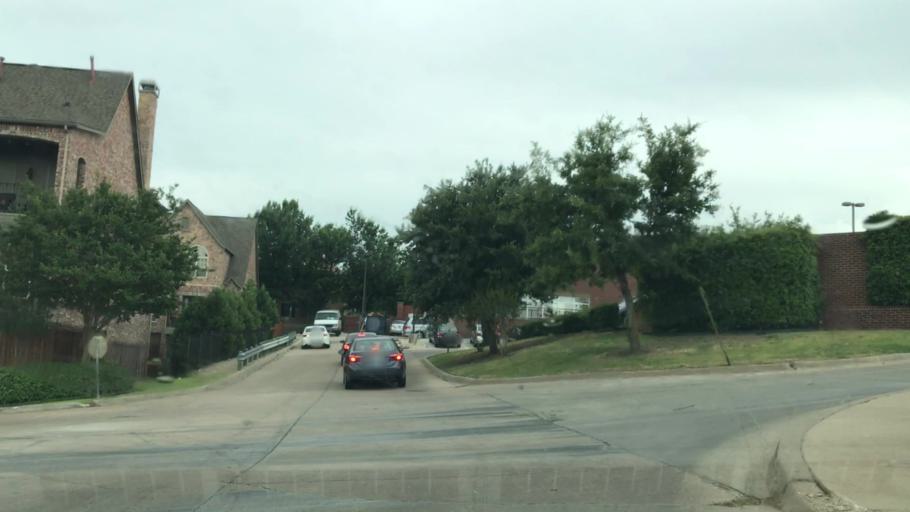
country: US
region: Texas
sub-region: Dallas County
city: Farmers Branch
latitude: 32.9185
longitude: -96.9574
